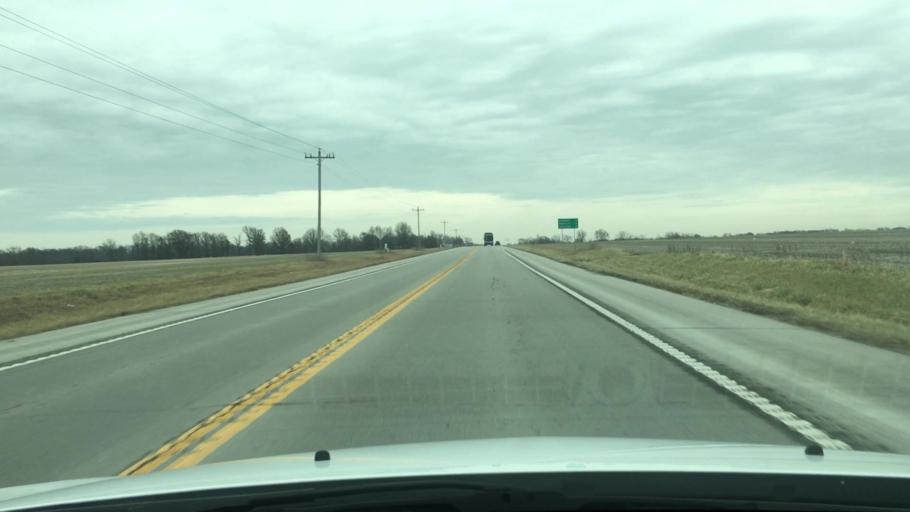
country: US
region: Missouri
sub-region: Audrain County
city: Mexico
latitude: 39.1637
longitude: -91.8166
